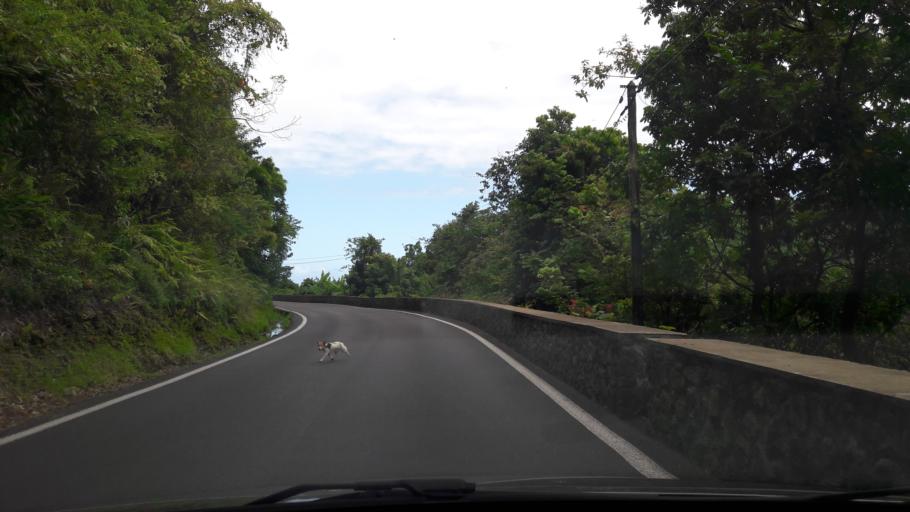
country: RE
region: Reunion
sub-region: Reunion
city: Saint-Andre
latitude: -20.9862
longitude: 55.6237
